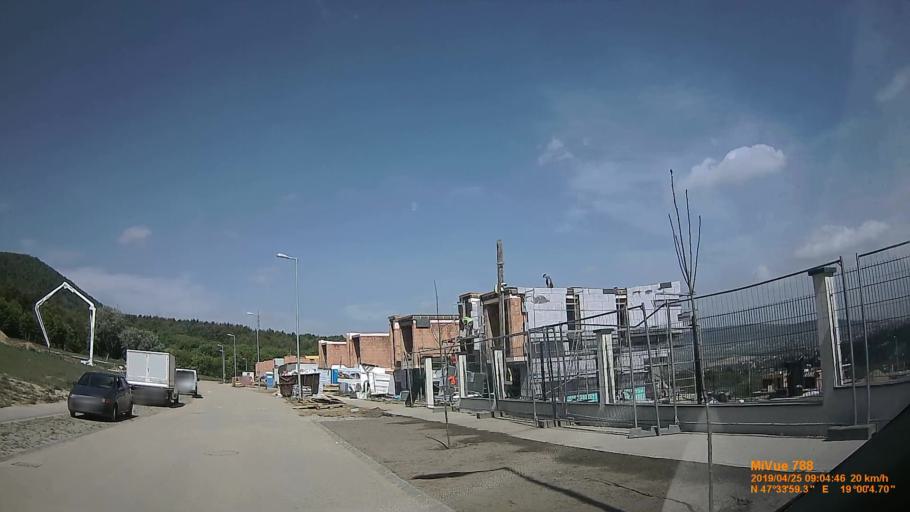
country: HU
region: Pest
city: Urom
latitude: 47.5665
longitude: 19.0012
